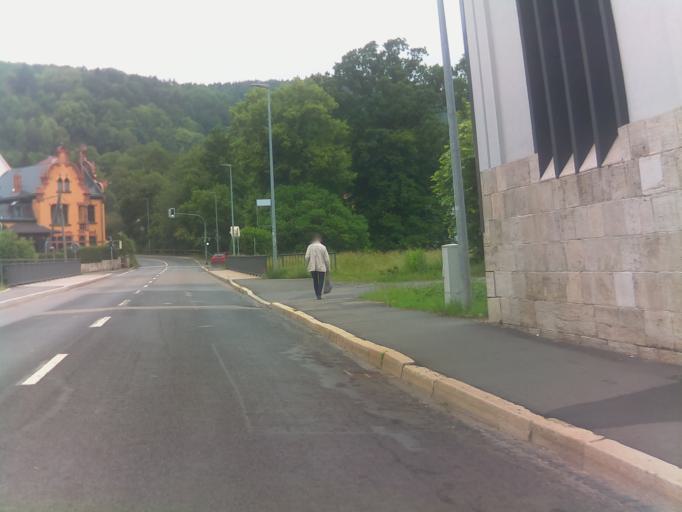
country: DE
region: Thuringia
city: Meiningen
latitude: 50.5753
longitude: 10.4127
